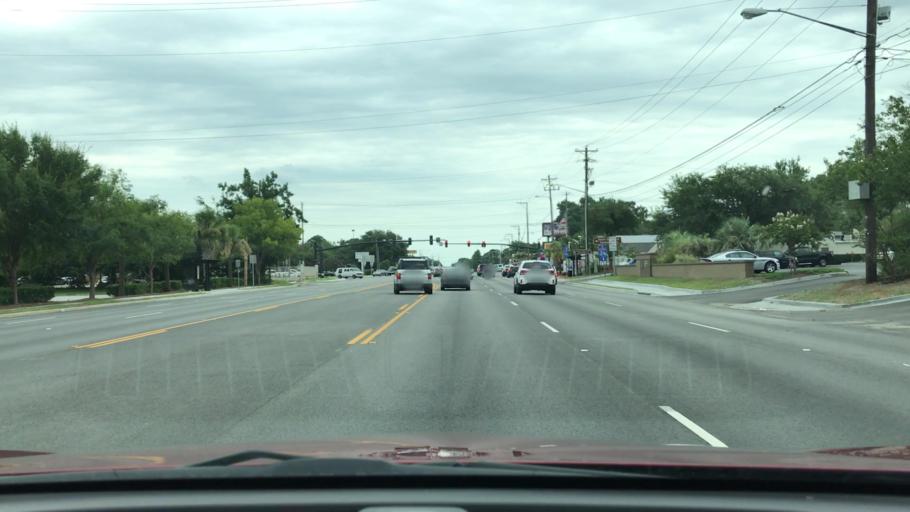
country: US
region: South Carolina
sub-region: Charleston County
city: North Charleston
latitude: 32.8010
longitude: -80.0183
